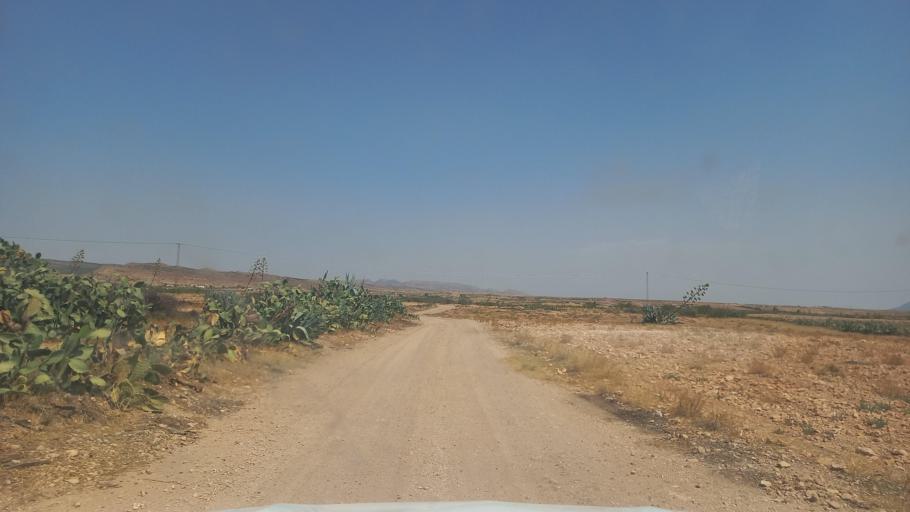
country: TN
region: Al Qasrayn
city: Kasserine
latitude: 35.2829
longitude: 8.9494
